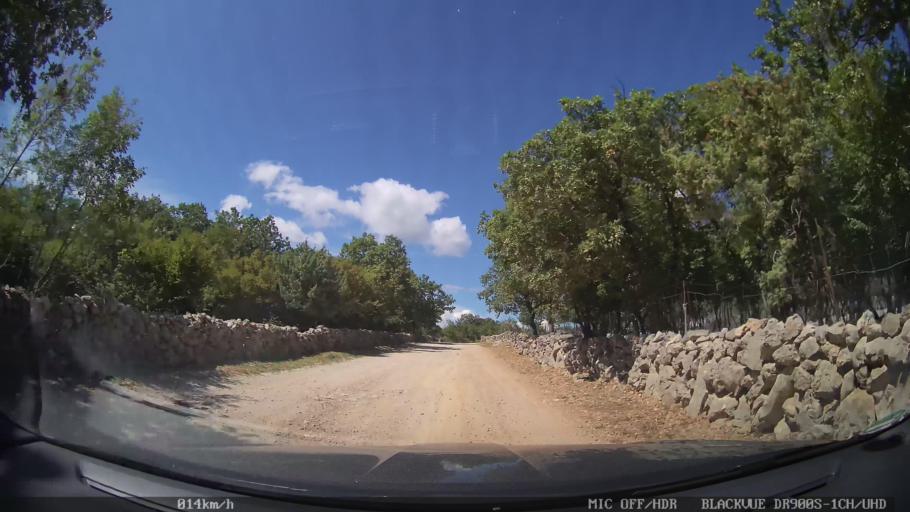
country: HR
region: Primorsko-Goranska
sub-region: Grad Krk
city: Krk
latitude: 45.0419
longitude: 14.5313
